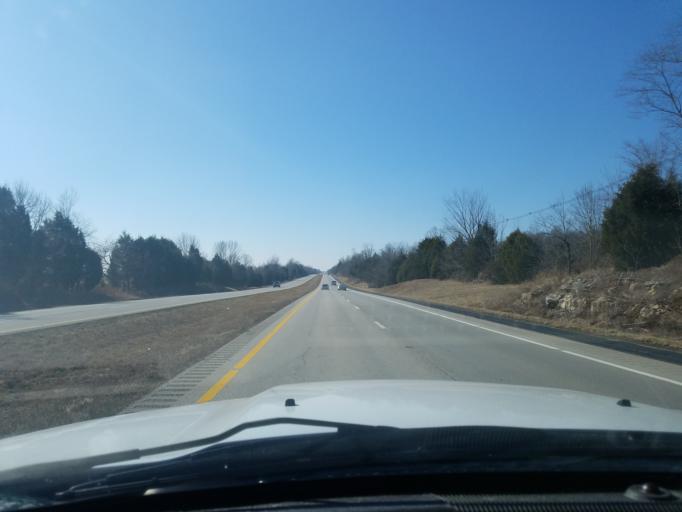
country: US
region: Kentucky
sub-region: Hardin County
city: Elizabethtown
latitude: 37.5972
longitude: -85.9904
